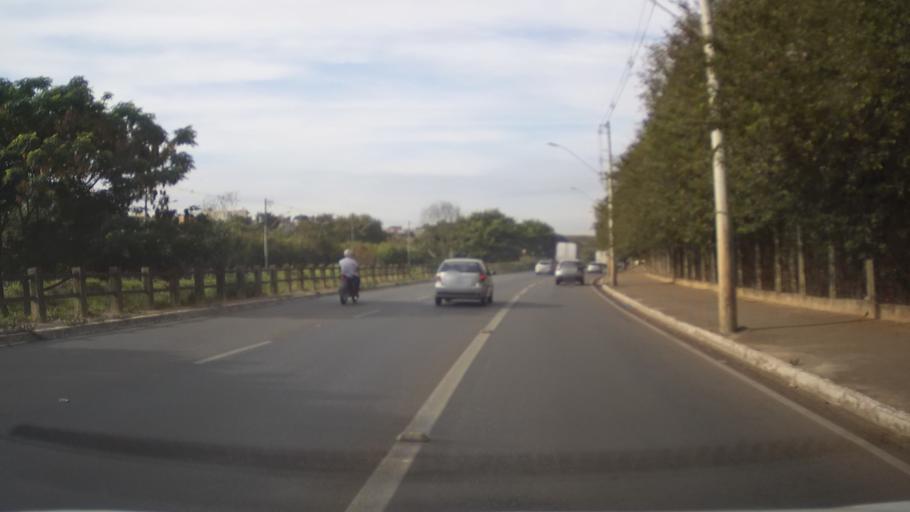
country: BR
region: Minas Gerais
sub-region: Contagem
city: Contagem
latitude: -19.8890
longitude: -44.0384
